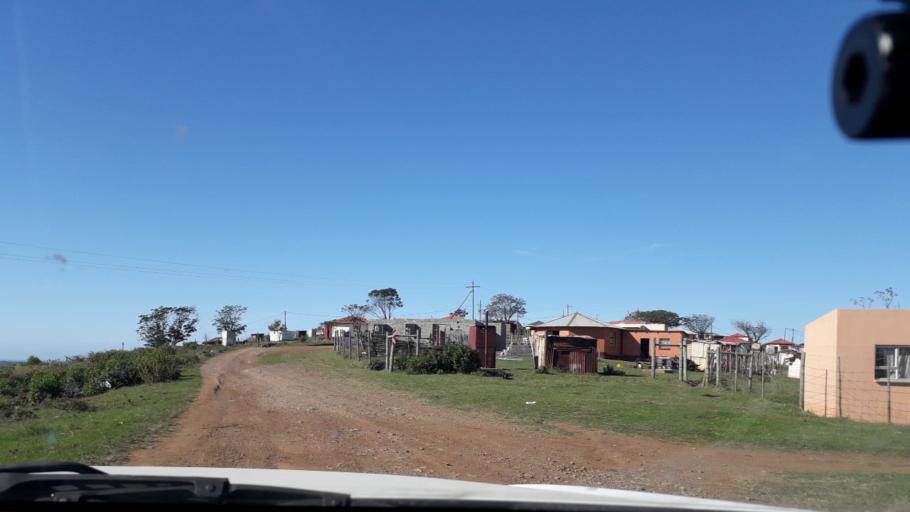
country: ZA
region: Eastern Cape
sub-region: Buffalo City Metropolitan Municipality
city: East London
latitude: -32.8420
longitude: 27.9857
